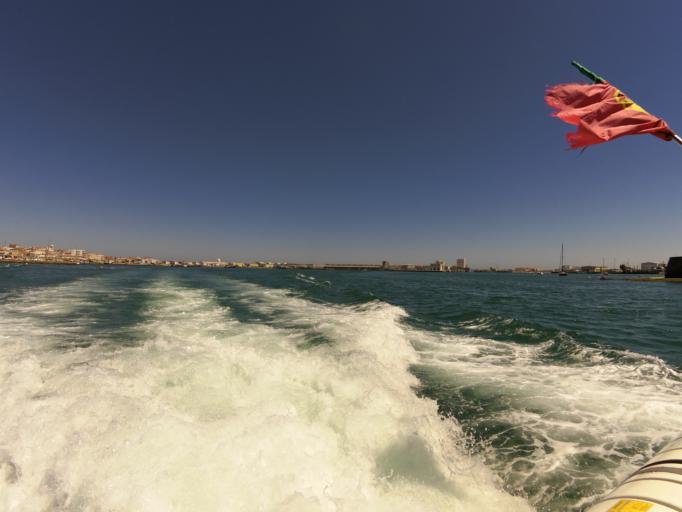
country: PT
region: Leiria
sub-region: Peniche
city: Peniche
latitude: 39.3494
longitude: -9.3752
